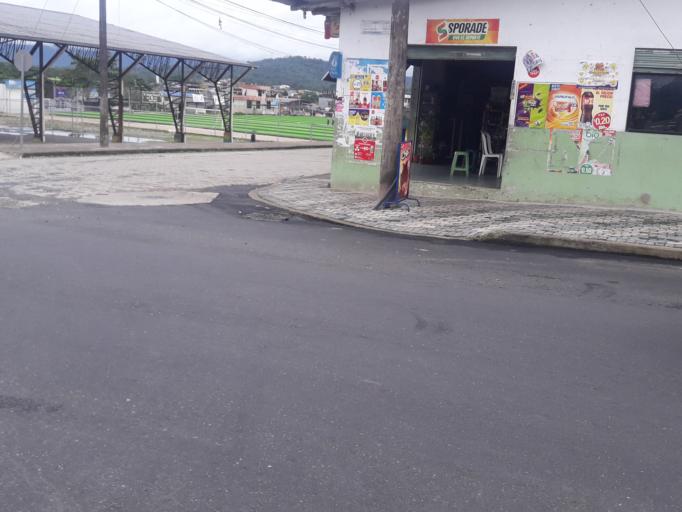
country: EC
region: Napo
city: Tena
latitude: -0.9994
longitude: -77.8094
